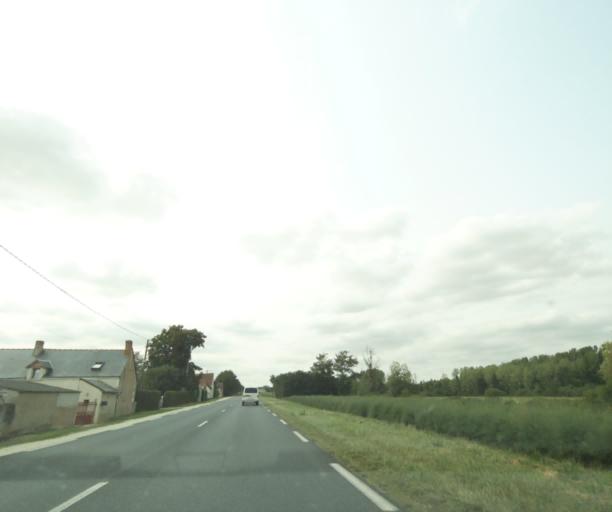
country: FR
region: Centre
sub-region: Departement de l'Indre
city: Chatillon-sur-Indre
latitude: 46.9985
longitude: 1.1529
